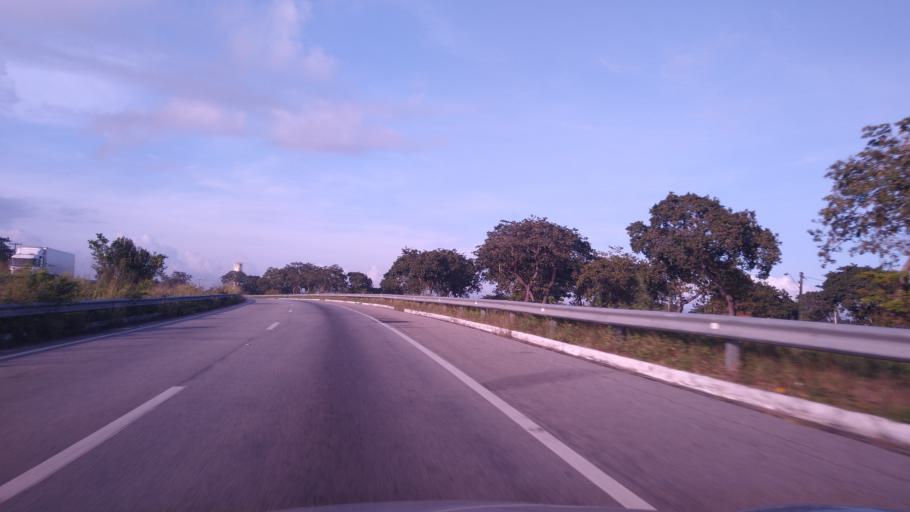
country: BR
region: Ceara
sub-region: Pacajus
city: Pacajus
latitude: -4.1690
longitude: -38.4930
